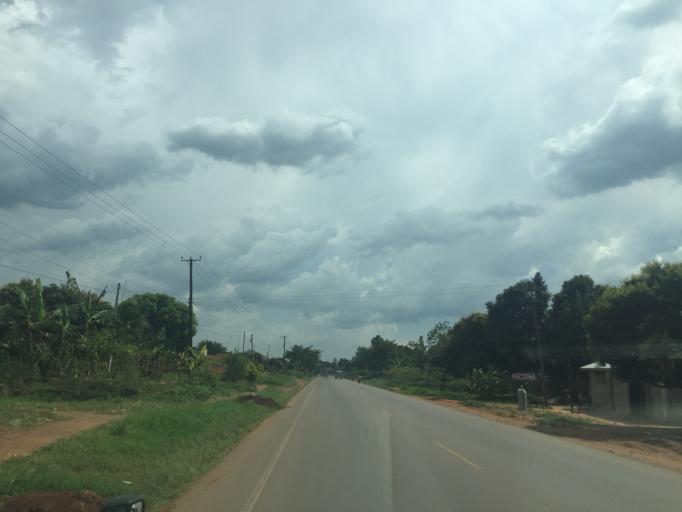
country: UG
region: Central Region
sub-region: Luwero District
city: Wobulenzi
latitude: 0.6889
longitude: 32.5229
